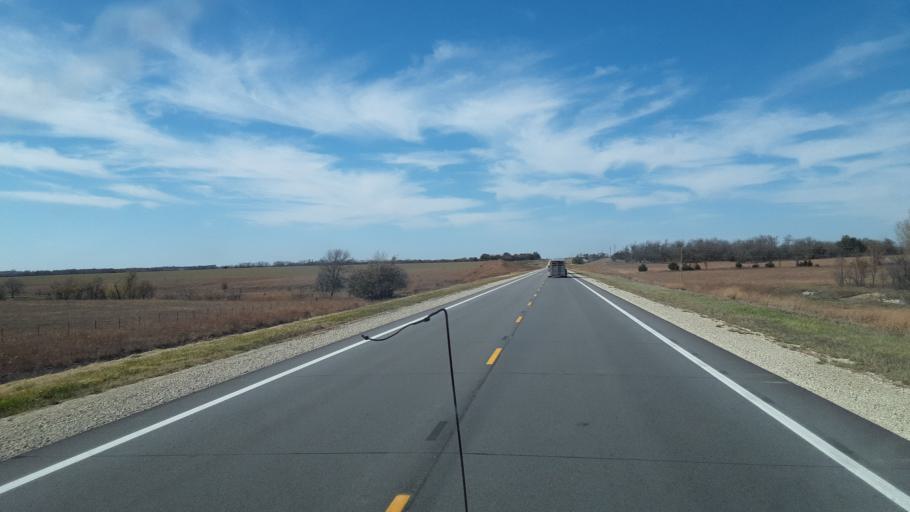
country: US
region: Kansas
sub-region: Marion County
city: Marion
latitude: 38.3624
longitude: -96.8486
